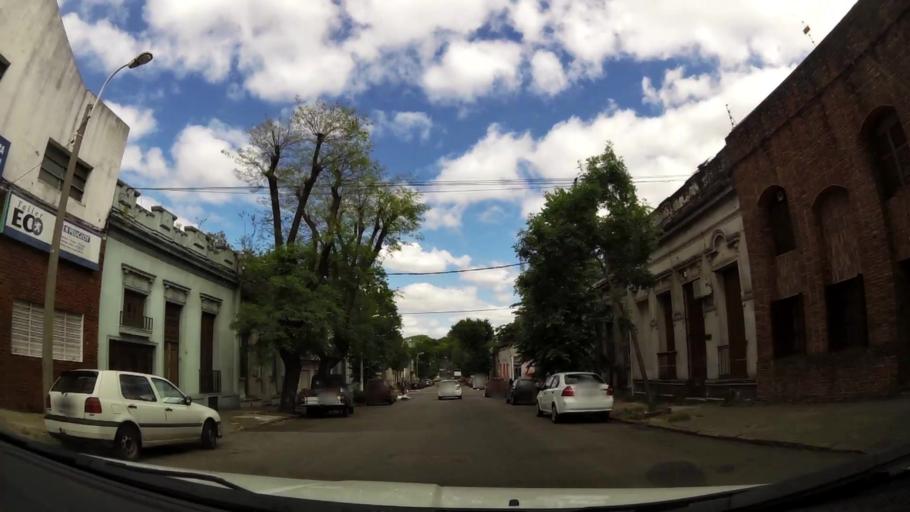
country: UY
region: Montevideo
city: Montevideo
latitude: -34.8787
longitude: -56.1822
